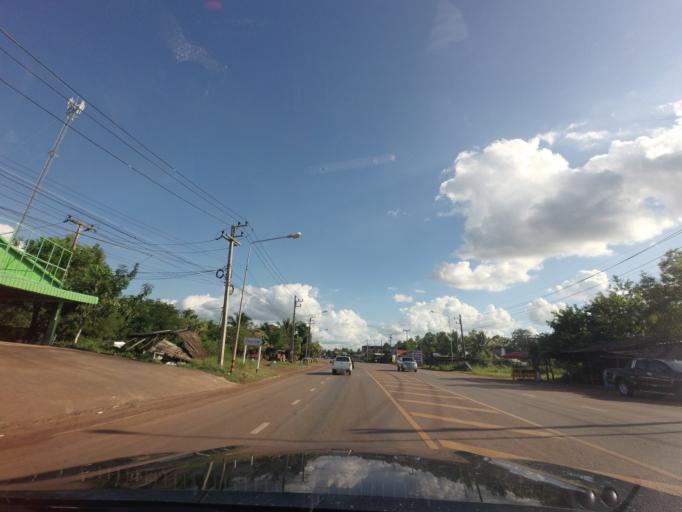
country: TH
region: Changwat Udon Thani
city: Ban Dung
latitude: 17.7108
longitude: 103.2502
